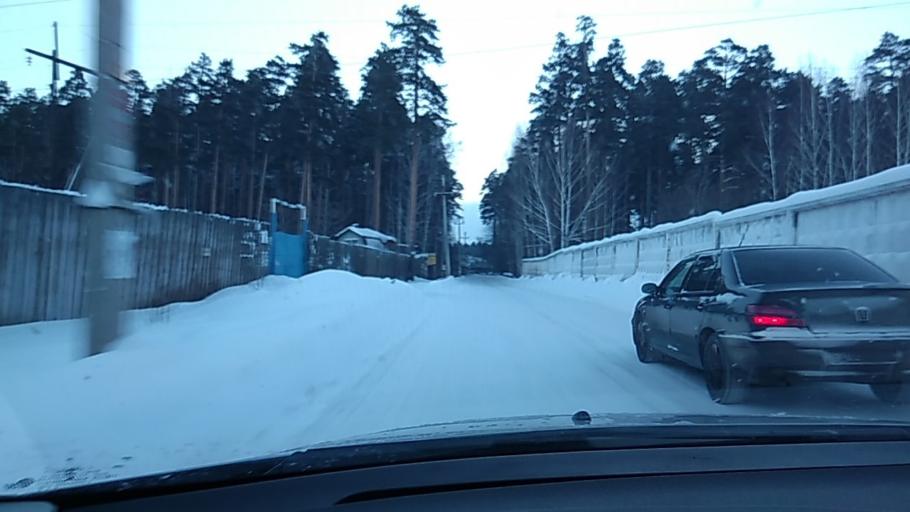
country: RU
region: Sverdlovsk
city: Verkhnyaya Pyshma
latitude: 56.9172
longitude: 60.5832
